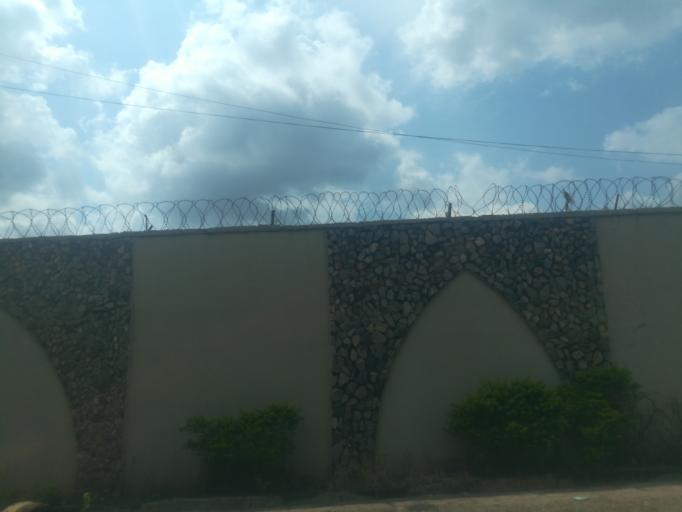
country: NG
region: Oyo
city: Ibadan
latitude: 7.3639
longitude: 3.8538
